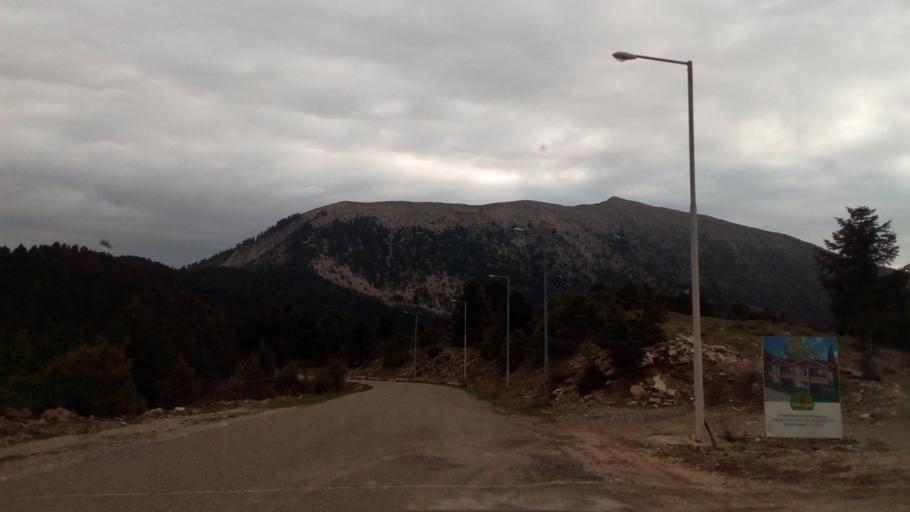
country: GR
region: West Greece
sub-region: Nomos Aitolias kai Akarnanias
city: Thermo
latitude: 38.6264
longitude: 21.8270
